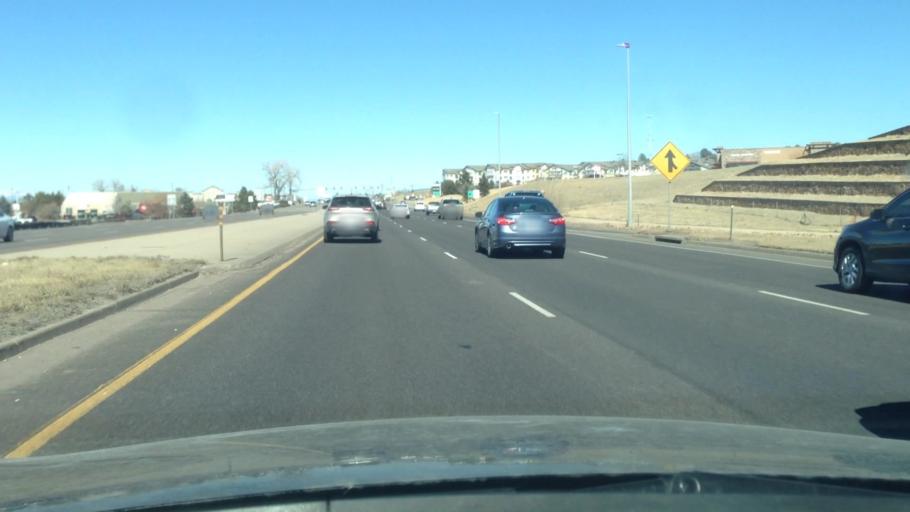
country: US
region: Colorado
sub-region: Douglas County
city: Stonegate
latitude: 39.5548
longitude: -104.7778
